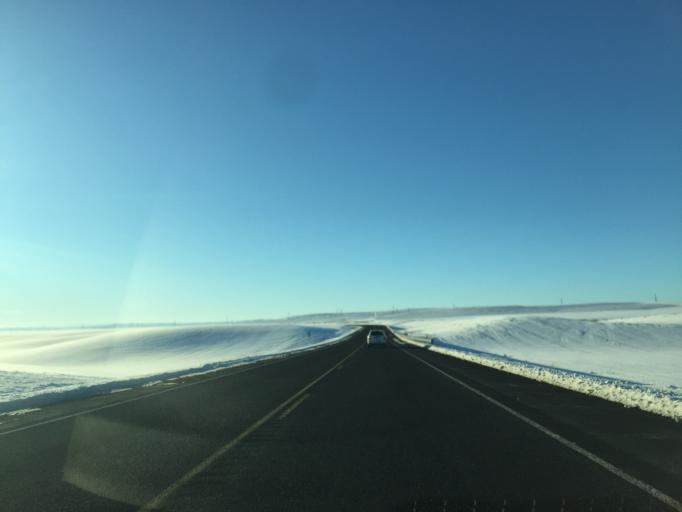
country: US
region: Washington
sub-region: Okanogan County
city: Coulee Dam
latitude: 47.6848
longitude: -119.1183
